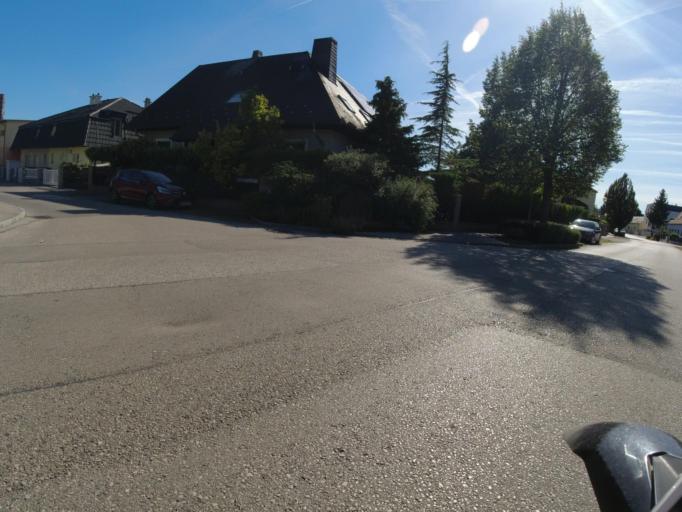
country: AT
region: Lower Austria
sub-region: Politischer Bezirk Modling
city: Guntramsdorf
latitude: 48.0294
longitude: 16.3061
